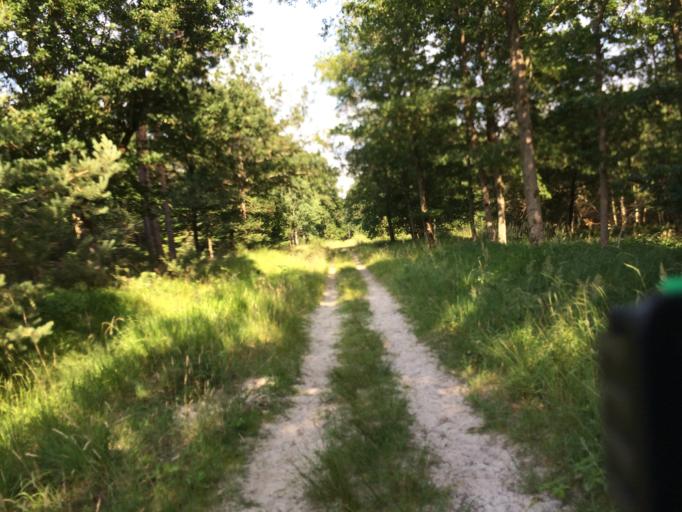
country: FR
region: Ile-de-France
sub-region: Departement de l'Essonne
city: Soisy-sur-Seine
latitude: 48.6676
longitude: 2.4759
